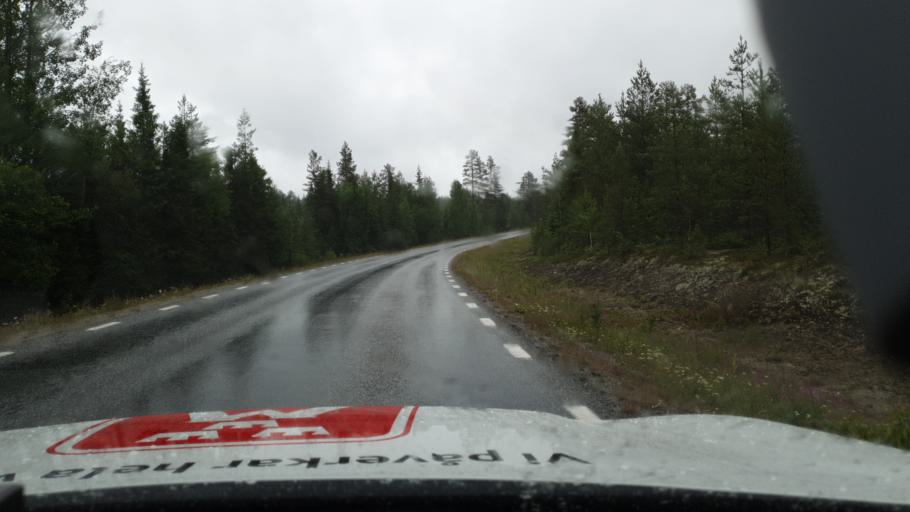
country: SE
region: Vaesterbotten
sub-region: Asele Kommun
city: Insjon
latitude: 64.3553
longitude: 17.9004
